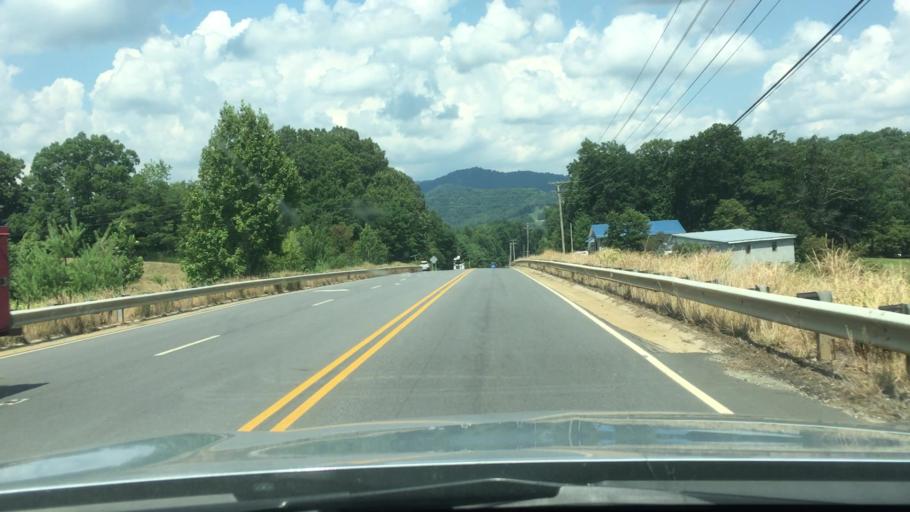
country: US
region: North Carolina
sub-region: Madison County
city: Marshall
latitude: 35.8227
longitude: -82.6316
